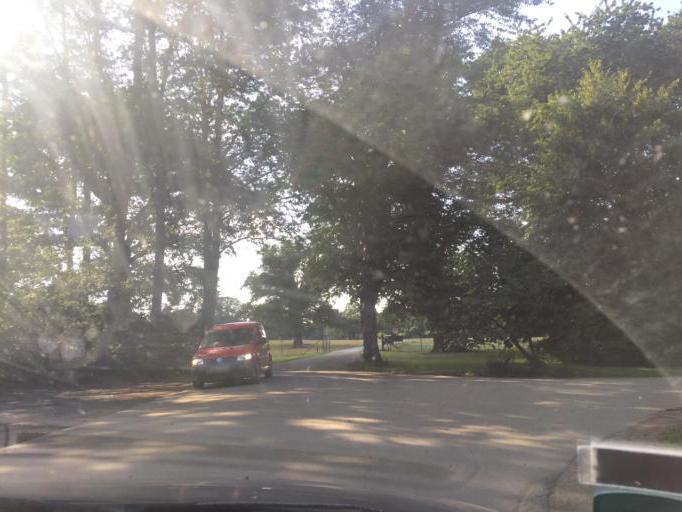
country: DK
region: Zealand
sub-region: Lolland Kommune
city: Maribo
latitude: 54.8250
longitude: 11.5066
